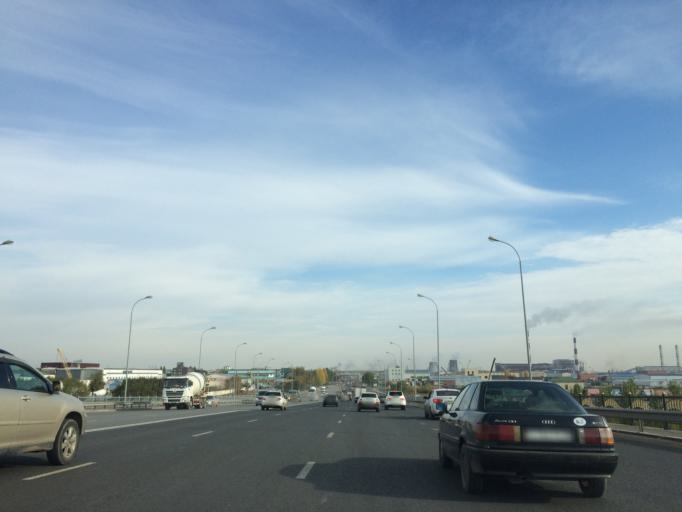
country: KZ
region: Astana Qalasy
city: Astana
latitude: 51.1734
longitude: 71.4832
